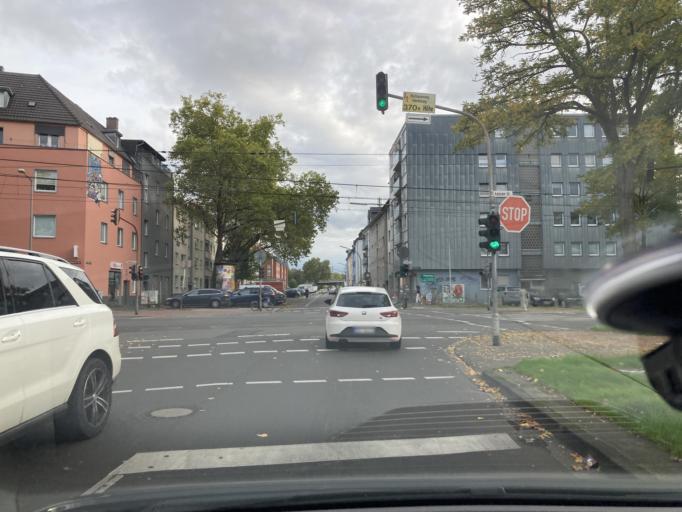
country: DE
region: North Rhine-Westphalia
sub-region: Regierungsbezirk Koln
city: Buchforst
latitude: 50.9504
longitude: 7.0013
